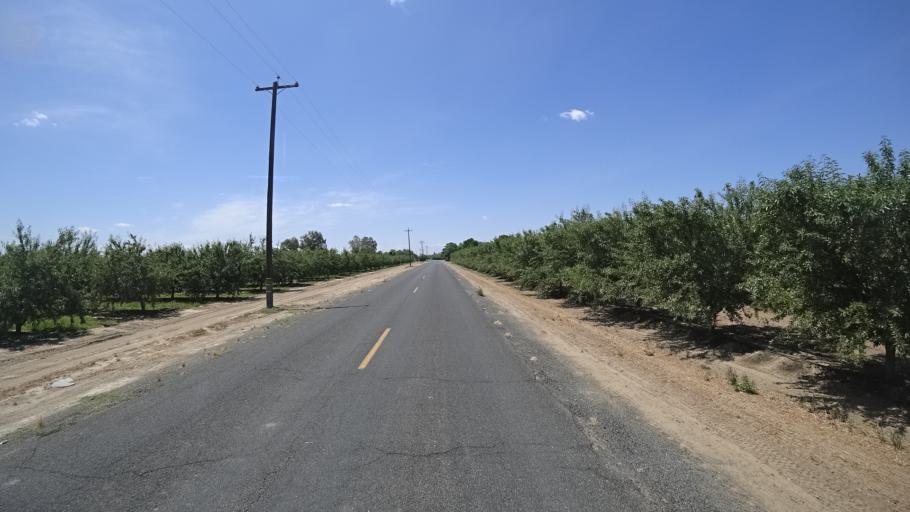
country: US
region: California
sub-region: Kings County
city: Lemoore
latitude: 36.2841
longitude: -119.7413
